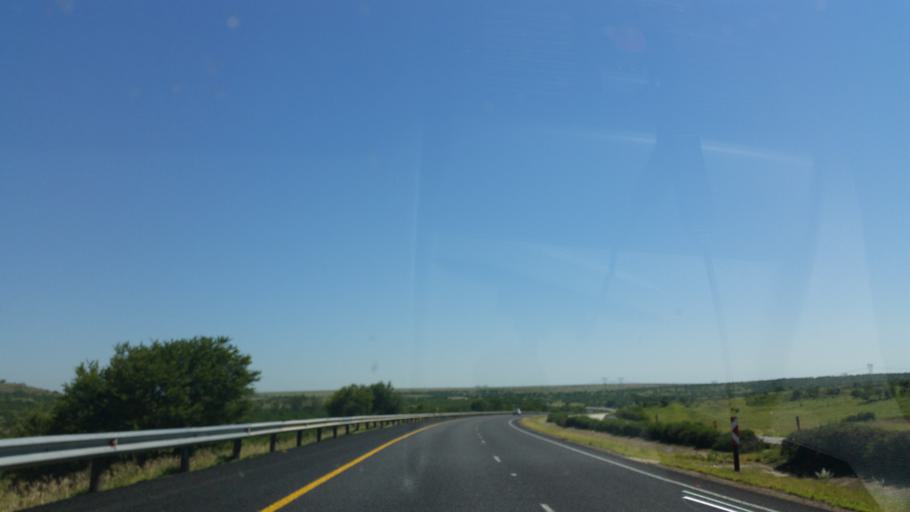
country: ZA
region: KwaZulu-Natal
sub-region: uThukela District Municipality
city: Ladysmith
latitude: -28.6821
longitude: 29.6324
